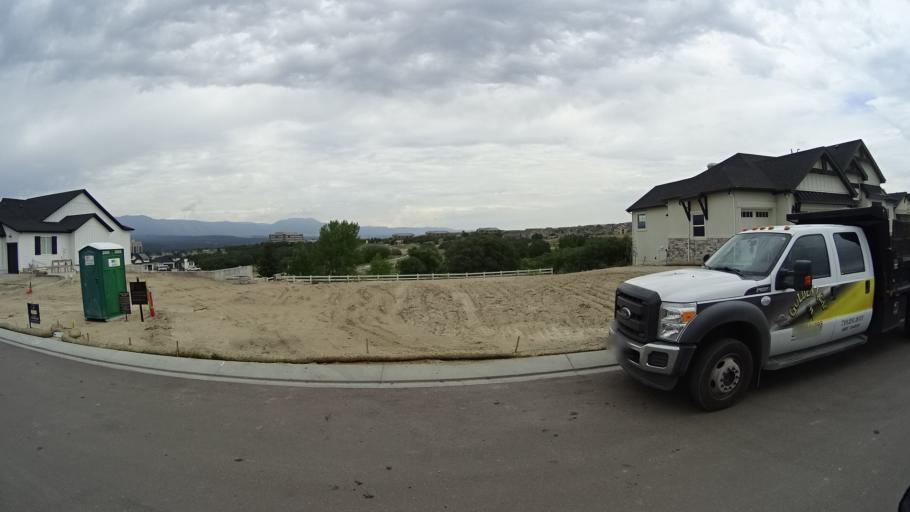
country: US
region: Colorado
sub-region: El Paso County
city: Gleneagle
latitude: 39.0061
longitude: -104.8108
